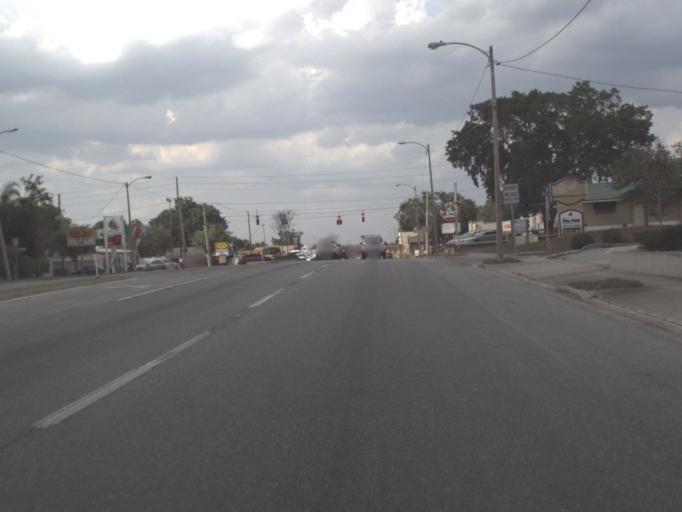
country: US
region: Florida
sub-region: Lake County
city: Eustis
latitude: 28.8406
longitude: -81.6854
